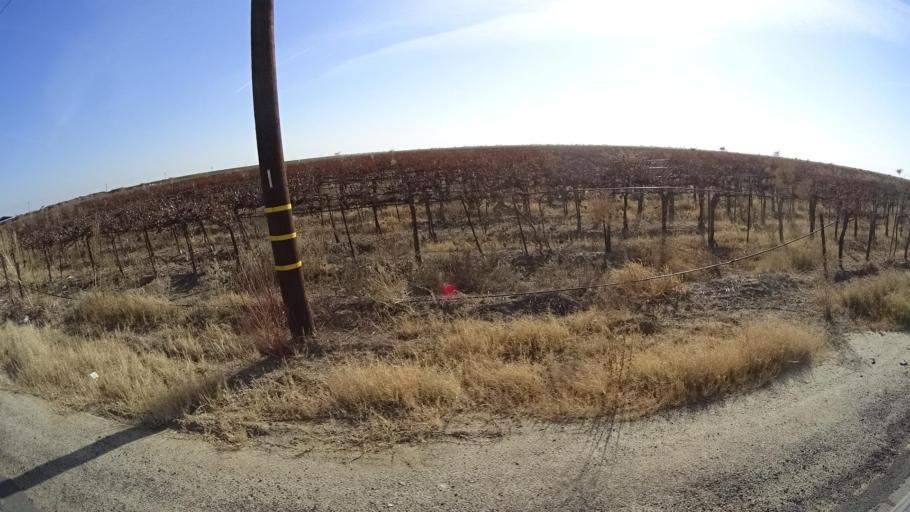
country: US
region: California
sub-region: Kern County
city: McFarland
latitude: 35.7032
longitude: -119.3338
